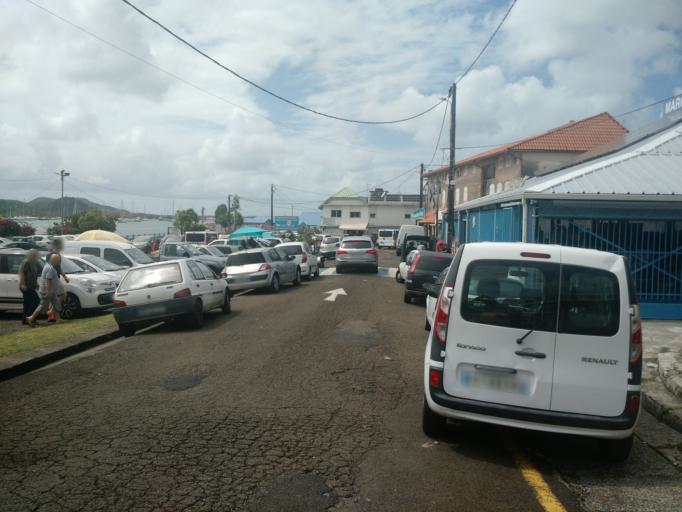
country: MQ
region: Martinique
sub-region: Martinique
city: Le Marin
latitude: 14.4706
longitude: -60.8699
